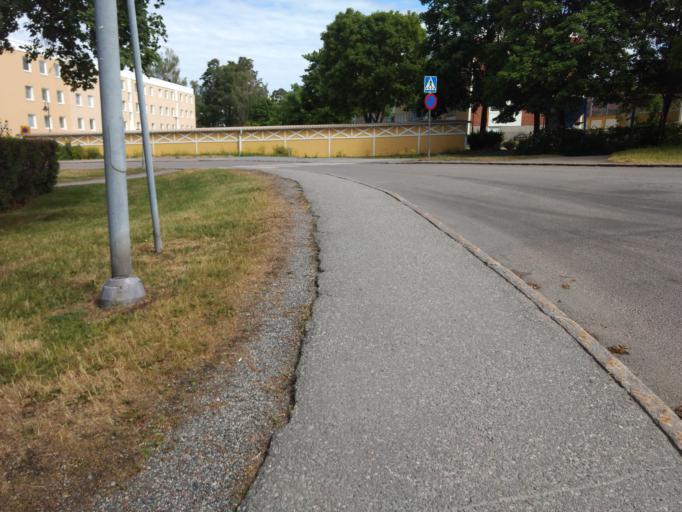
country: SE
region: Stockholm
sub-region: Upplands Vasby Kommun
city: Upplands Vaesby
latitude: 59.5216
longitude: 17.9161
